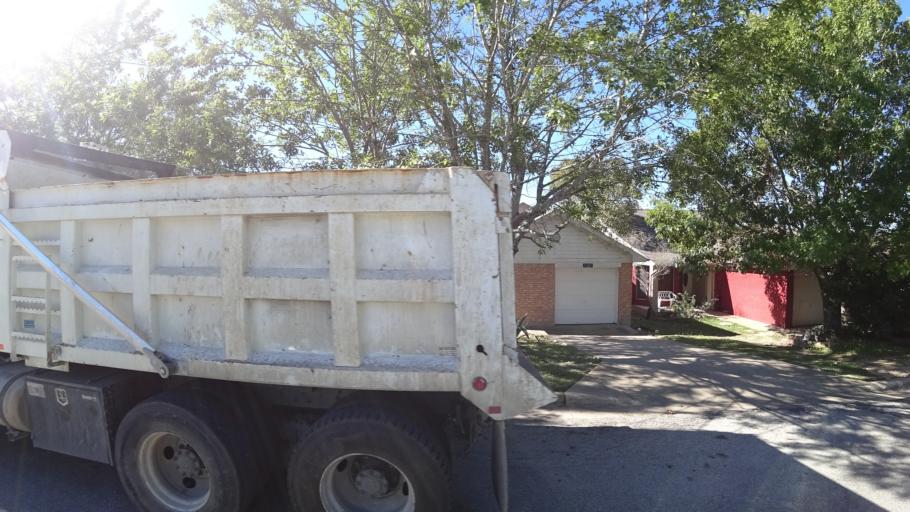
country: US
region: Texas
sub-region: Travis County
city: Manor
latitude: 30.3340
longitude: -97.6473
